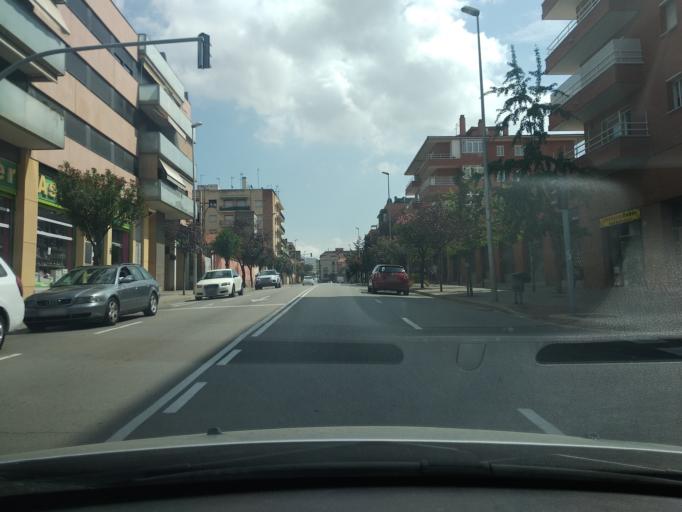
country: ES
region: Catalonia
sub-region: Provincia de Barcelona
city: Canovelles
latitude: 41.6140
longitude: 2.2875
